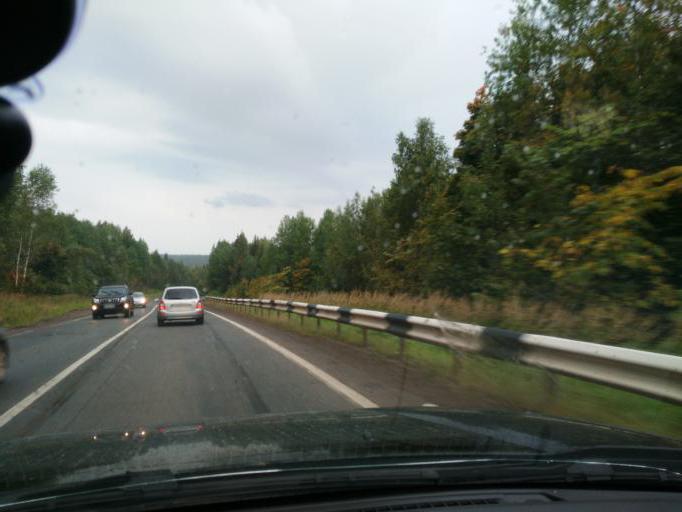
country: RU
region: Perm
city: Barda
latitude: 56.8907
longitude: 55.7666
